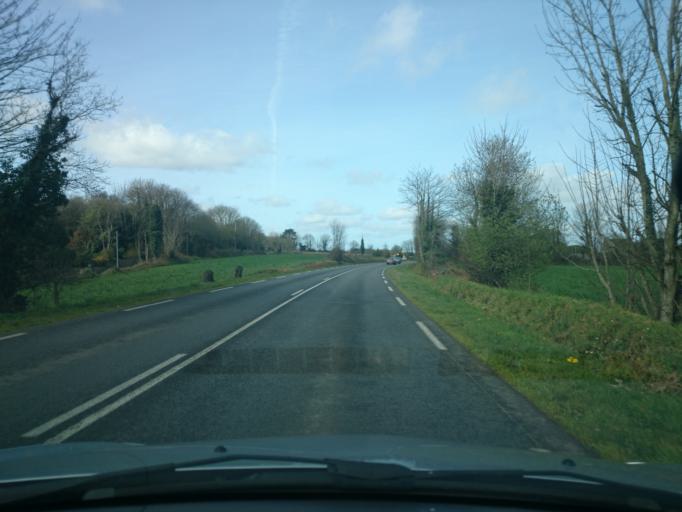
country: FR
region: Brittany
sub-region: Departement du Finistere
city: Gouesnou
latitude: 48.4411
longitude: -4.4487
